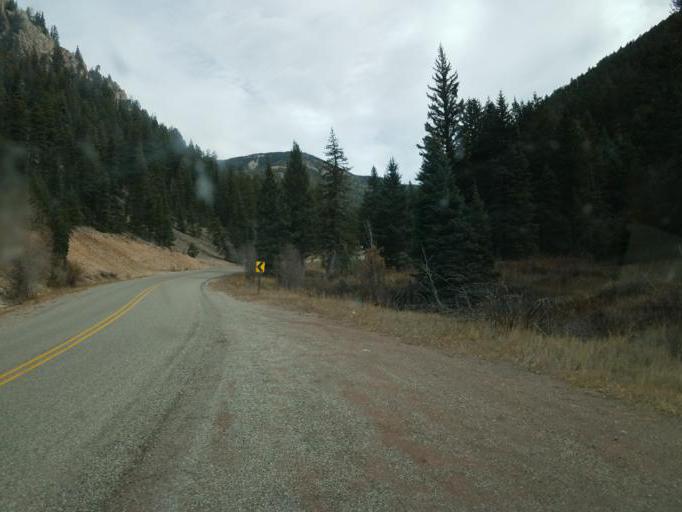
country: US
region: New Mexico
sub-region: Taos County
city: Arroyo Seco
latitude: 36.5883
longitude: -105.4919
